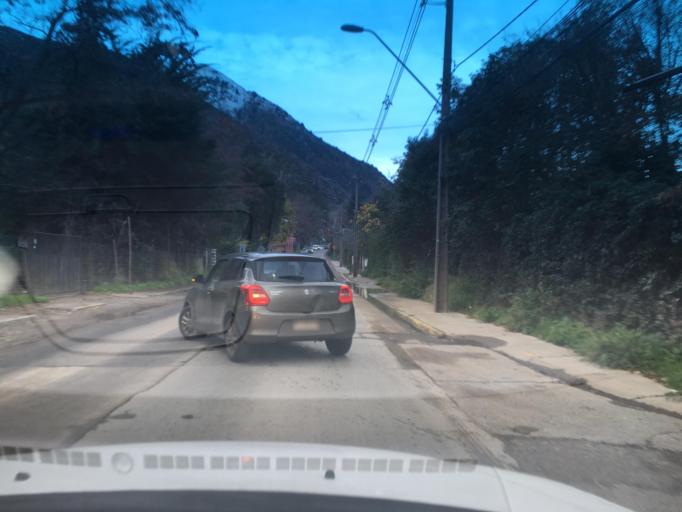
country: CL
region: Santiago Metropolitan
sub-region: Provincia de Cordillera
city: Puente Alto
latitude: -33.5760
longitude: -70.4493
